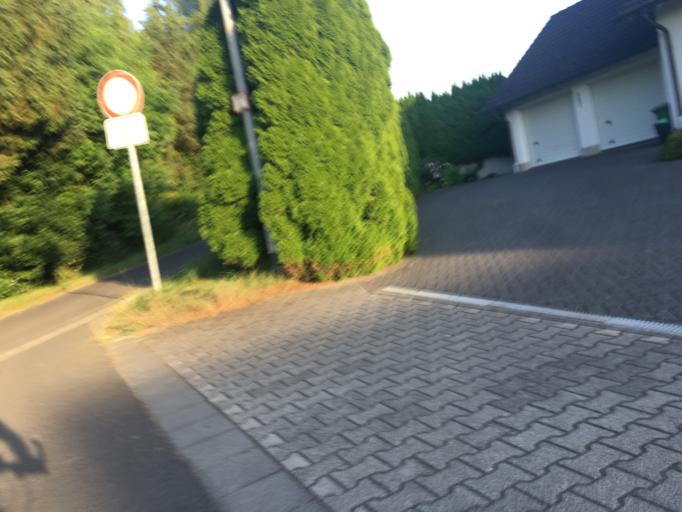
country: DE
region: Hesse
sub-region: Regierungsbezirk Darmstadt
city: Gelnhausen
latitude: 50.1823
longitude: 9.1679
